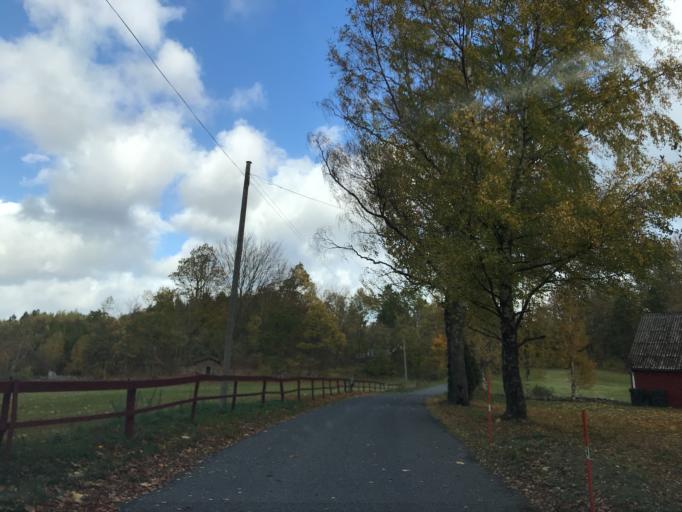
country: SE
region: Skane
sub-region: Perstorps Kommun
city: Perstorp
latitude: 56.0333
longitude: 13.3942
